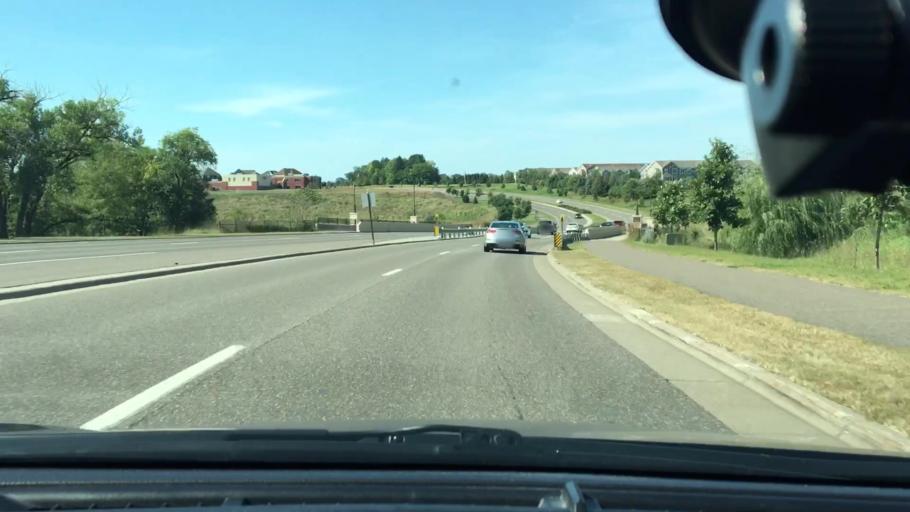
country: US
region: Minnesota
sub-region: Hennepin County
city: Maple Grove
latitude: 45.0844
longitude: -93.4906
